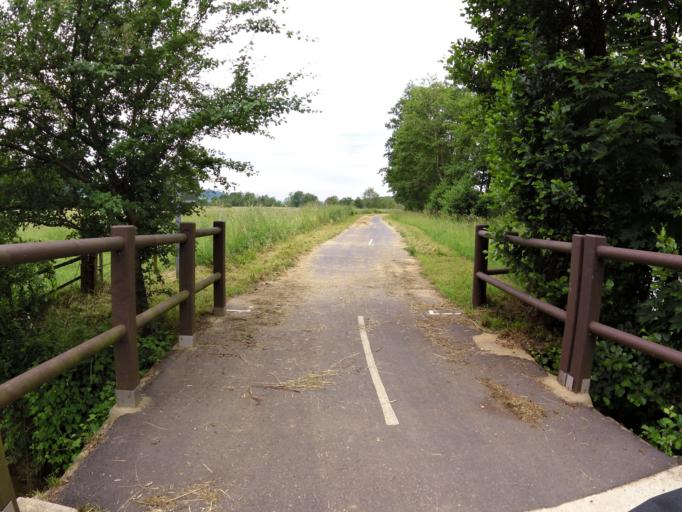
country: FR
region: Champagne-Ardenne
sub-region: Departement des Ardennes
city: Donchery
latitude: 49.6971
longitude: 4.8406
